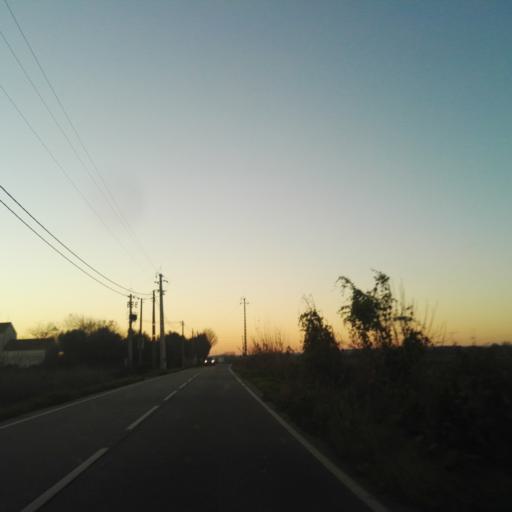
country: PT
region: Santarem
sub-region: Alpiarca
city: Alpiarca
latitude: 39.3027
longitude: -8.5381
